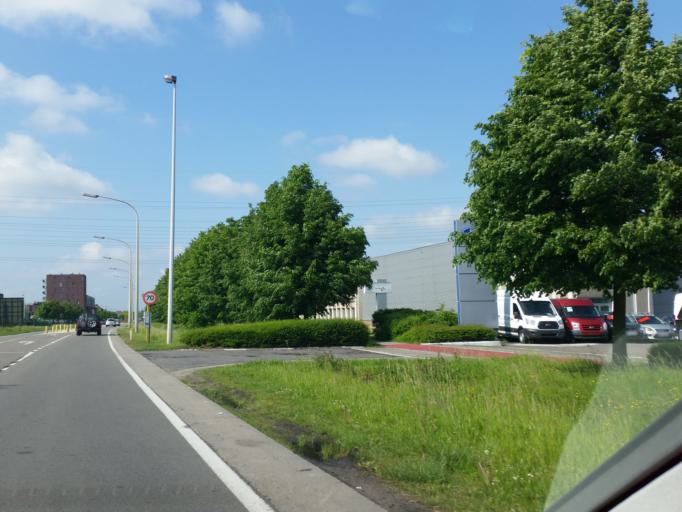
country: BE
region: Flanders
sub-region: Provincie Vlaams-Brabant
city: Vilvoorde
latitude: 50.9449
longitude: 4.4428
